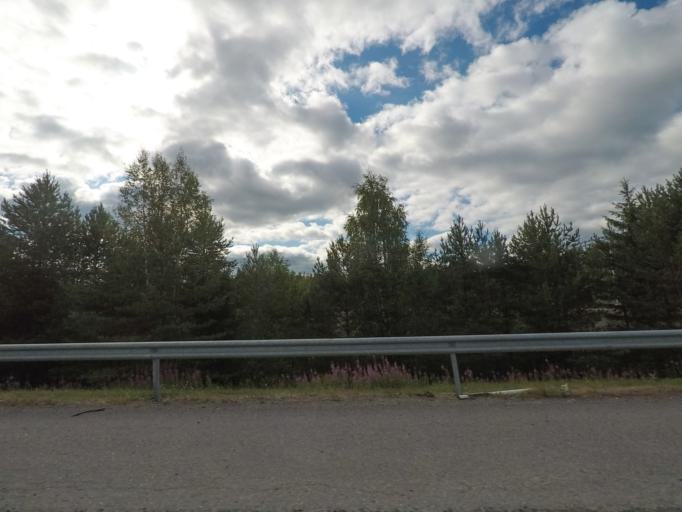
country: FI
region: Uusimaa
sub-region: Porvoo
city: Pukkila
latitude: 60.7949
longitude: 25.4915
